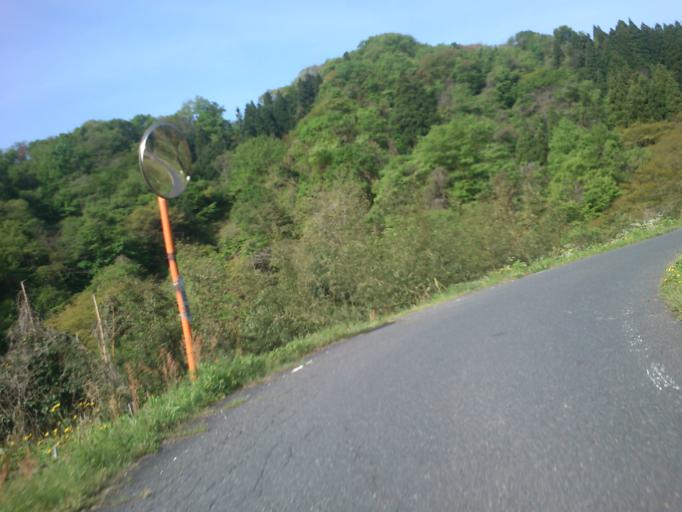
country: JP
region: Kyoto
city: Miyazu
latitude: 35.6370
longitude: 135.1899
